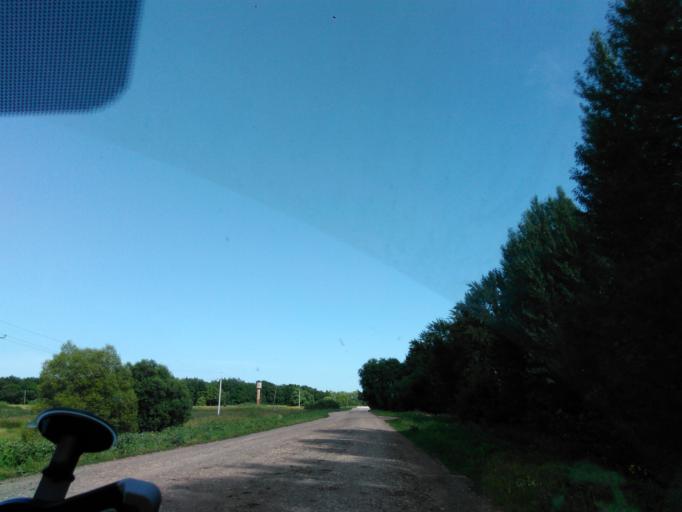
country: RU
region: Penza
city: Lermontovo
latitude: 52.9835
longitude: 43.6593
